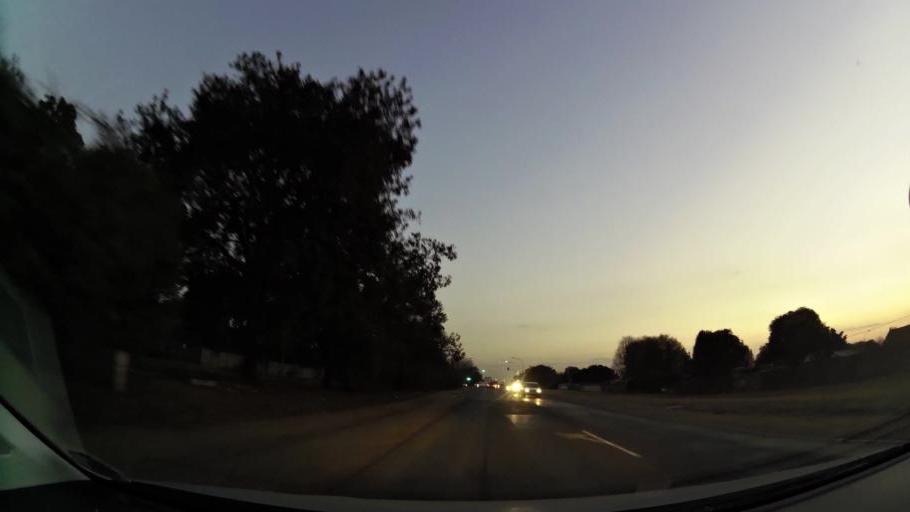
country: ZA
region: Gauteng
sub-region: Ekurhuleni Metropolitan Municipality
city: Tembisa
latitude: -26.0614
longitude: 28.2254
